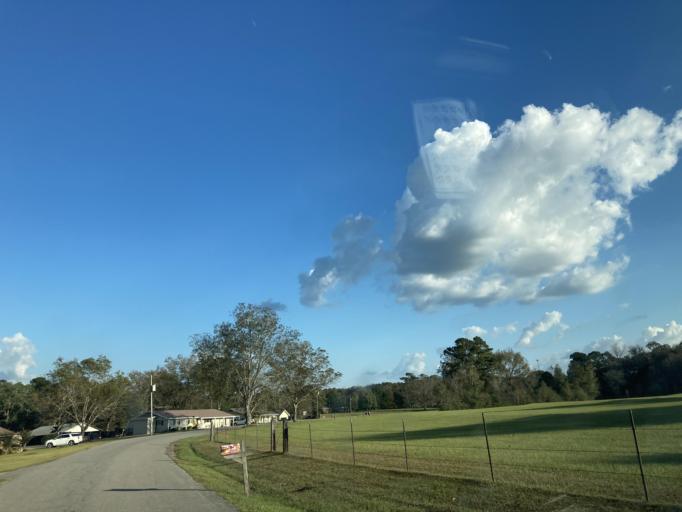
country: US
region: Mississippi
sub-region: Lamar County
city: Sumrall
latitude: 31.3890
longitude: -89.6386
